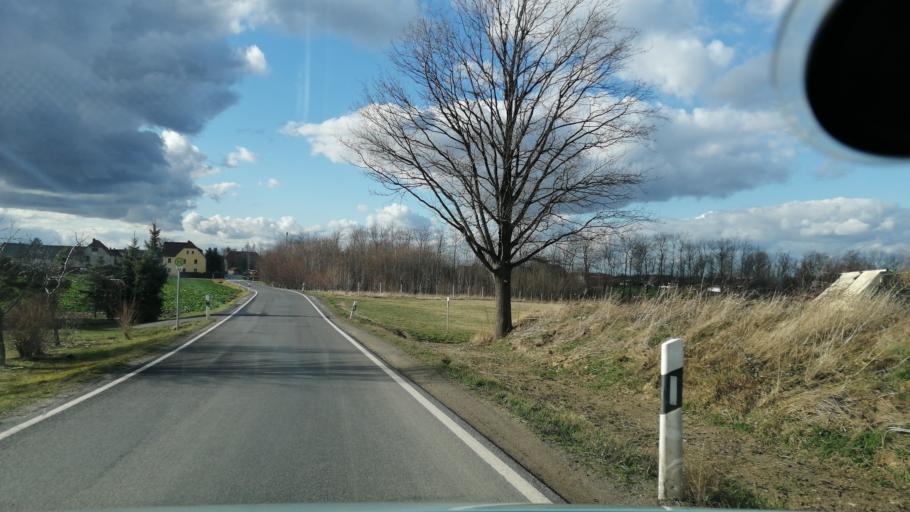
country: DE
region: Saxony
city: Grosspostwitz
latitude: 51.1415
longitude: 14.4463
